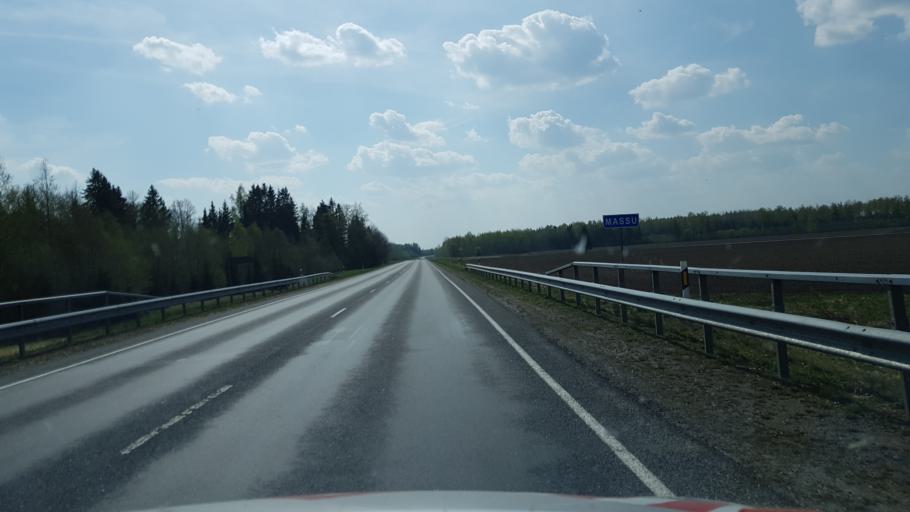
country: EE
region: Paernumaa
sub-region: Vaendra vald (alev)
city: Vandra
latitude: 58.6386
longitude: 24.9636
